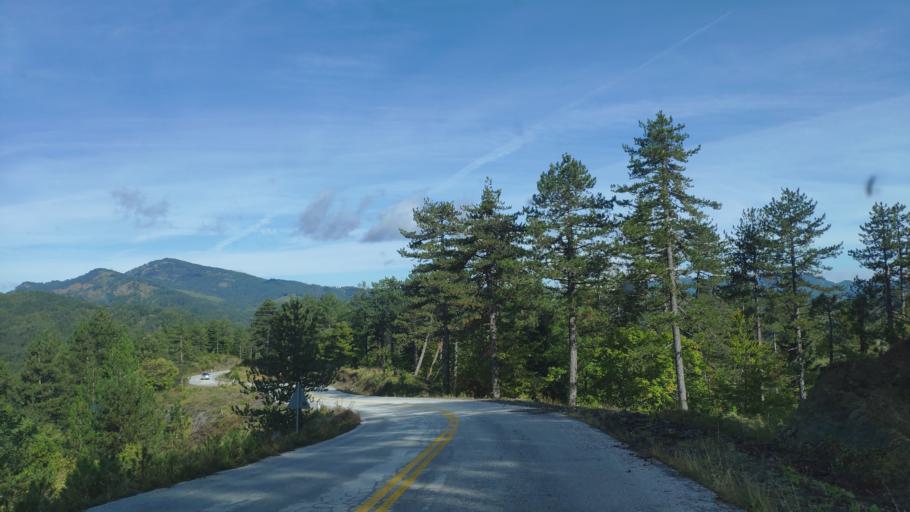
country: GR
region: West Macedonia
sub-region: Nomos Kastorias
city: Nestorio
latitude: 40.3647
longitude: 20.9472
